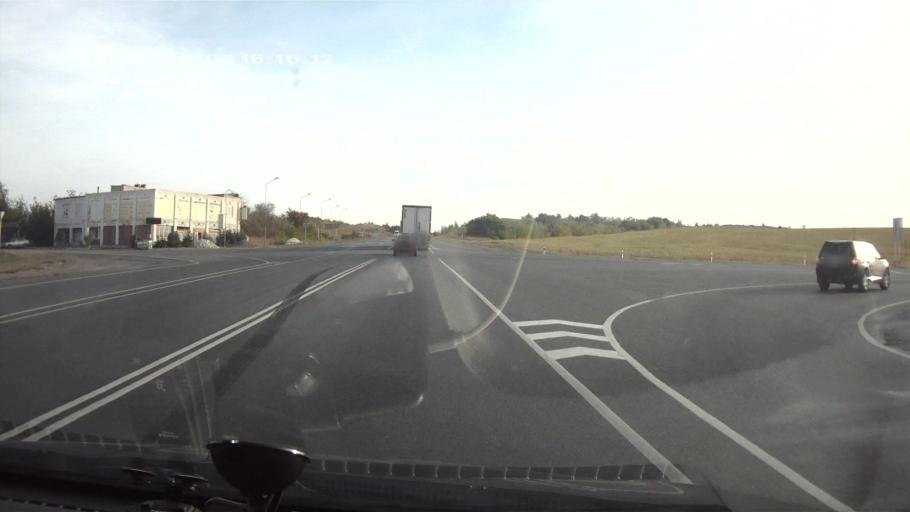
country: RU
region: Saratov
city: Sokolovyy
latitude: 51.6060
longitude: 45.7719
